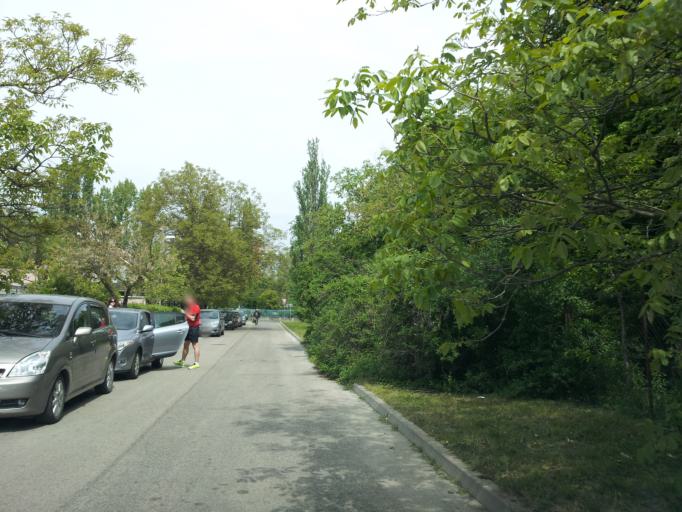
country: HU
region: Pest
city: Budakalasz
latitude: 47.5937
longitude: 19.0651
